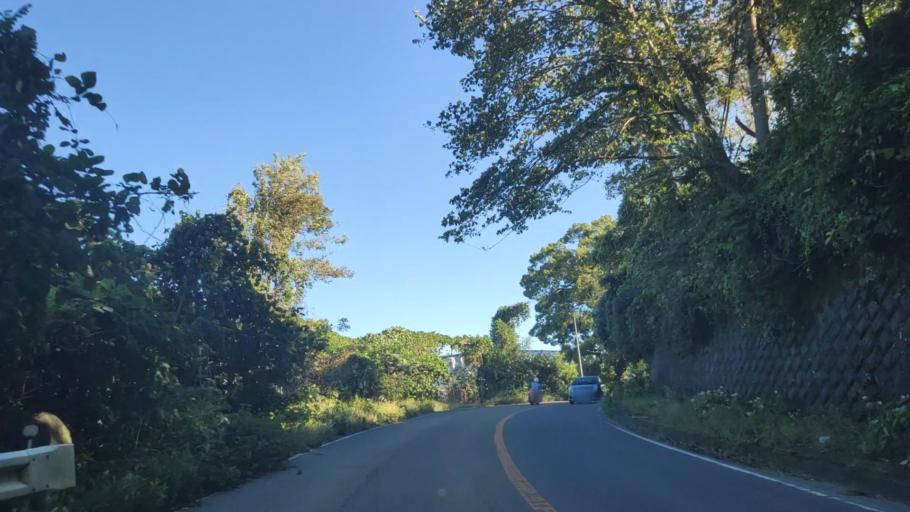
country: JP
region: Tokyo
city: Hachioji
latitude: 35.5684
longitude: 139.3112
